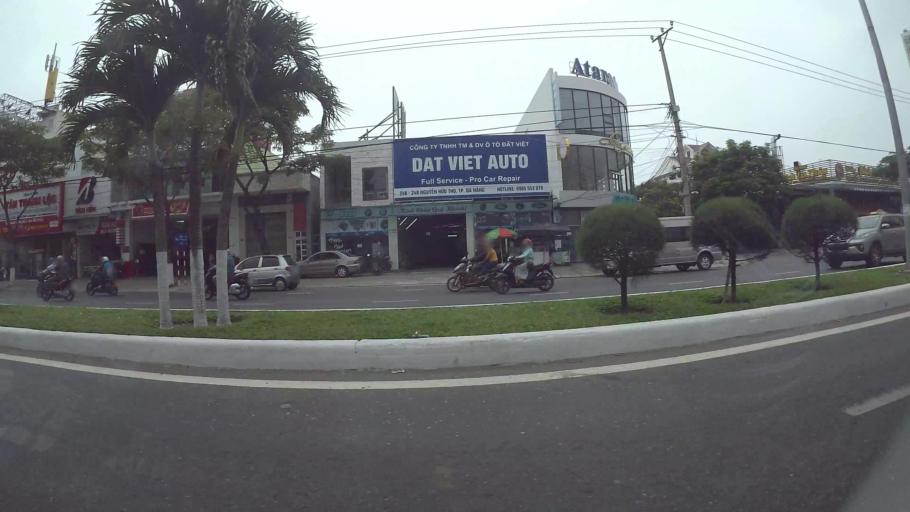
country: VN
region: Da Nang
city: Cam Le
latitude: 16.0382
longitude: 108.2104
